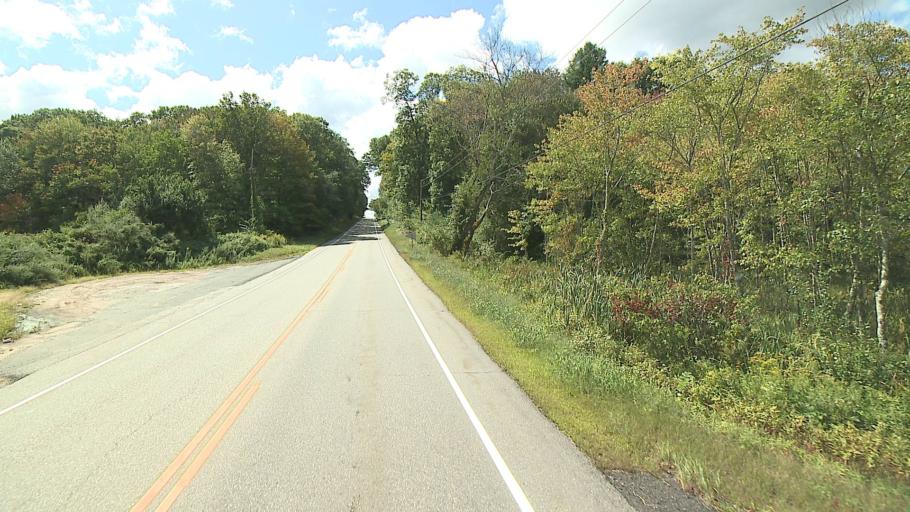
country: US
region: Connecticut
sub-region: Tolland County
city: Storrs
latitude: 41.8168
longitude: -72.2919
